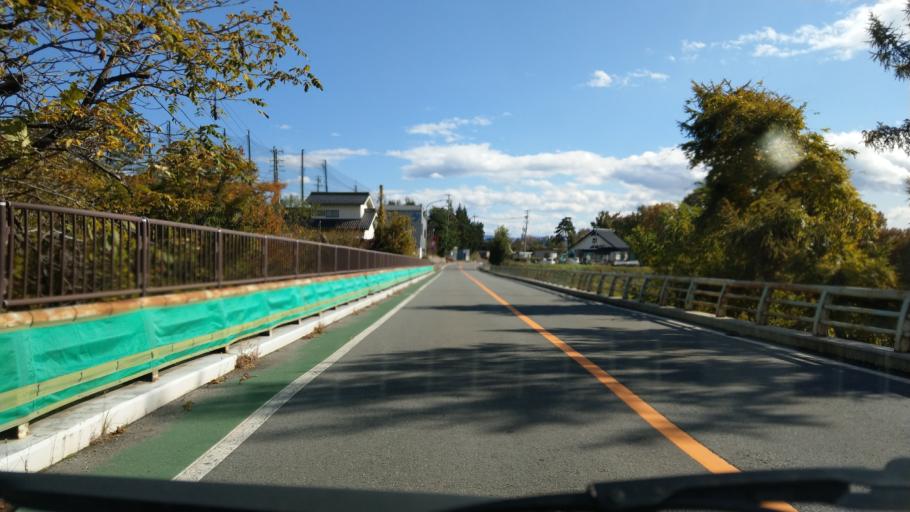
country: JP
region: Nagano
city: Komoro
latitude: 36.3077
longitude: 138.4287
